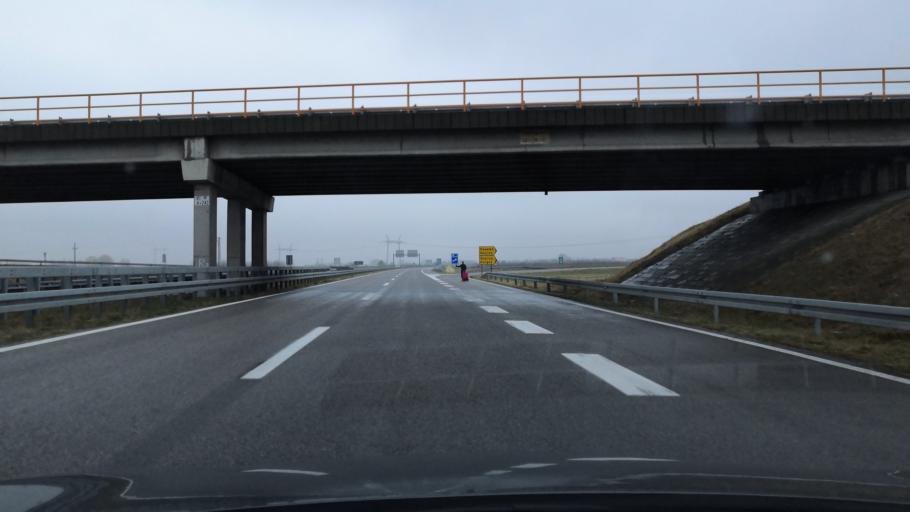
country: HU
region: Csongrad
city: Morahalom
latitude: 46.1536
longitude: 19.9372
